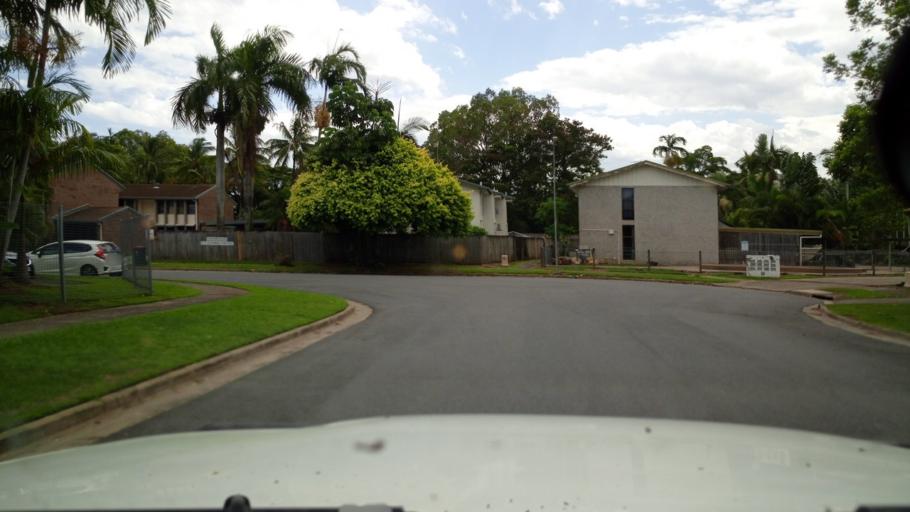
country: AU
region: Queensland
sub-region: Cairns
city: Cairns
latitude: -16.9159
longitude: 145.7400
